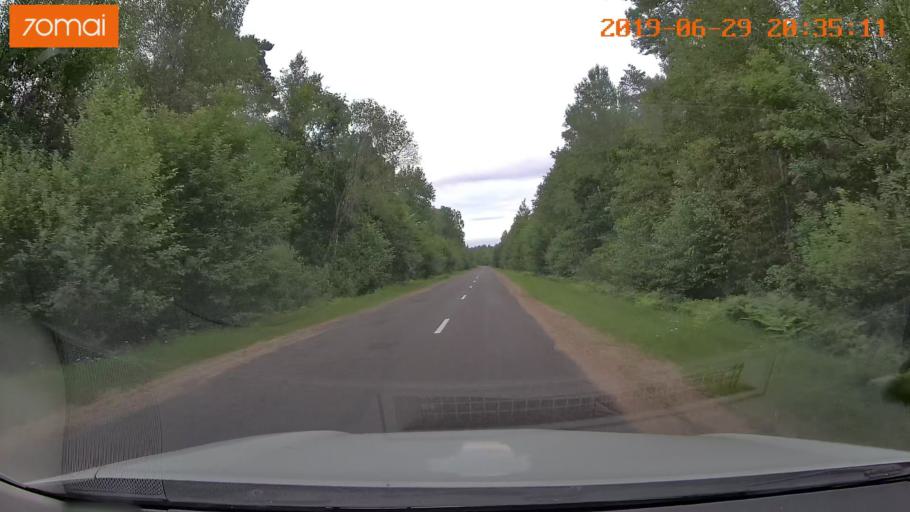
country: BY
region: Brest
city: Hantsavichy
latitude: 52.5150
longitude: 26.3463
